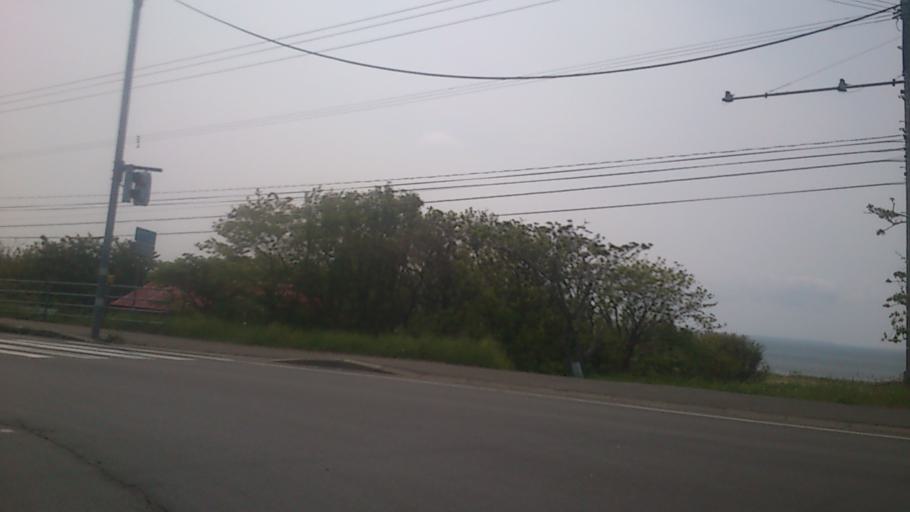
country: JP
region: Hokkaido
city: Nemuro
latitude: 43.2820
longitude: 145.5074
